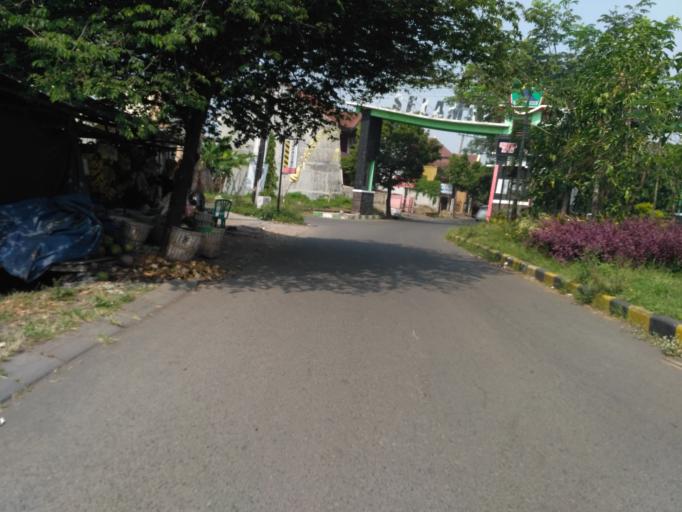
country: ID
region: East Java
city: Malang
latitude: -7.9710
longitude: 112.6641
